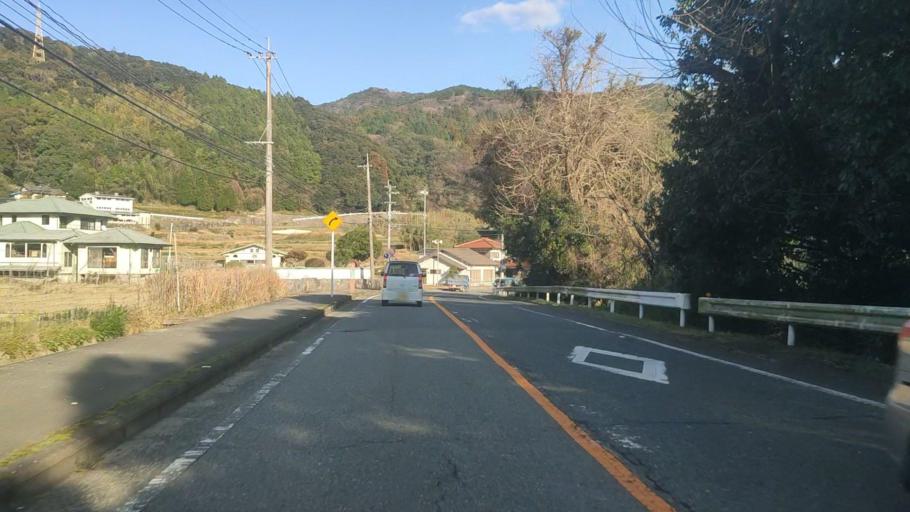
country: JP
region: Saga Prefecture
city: Saga-shi
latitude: 33.3430
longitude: 130.2506
